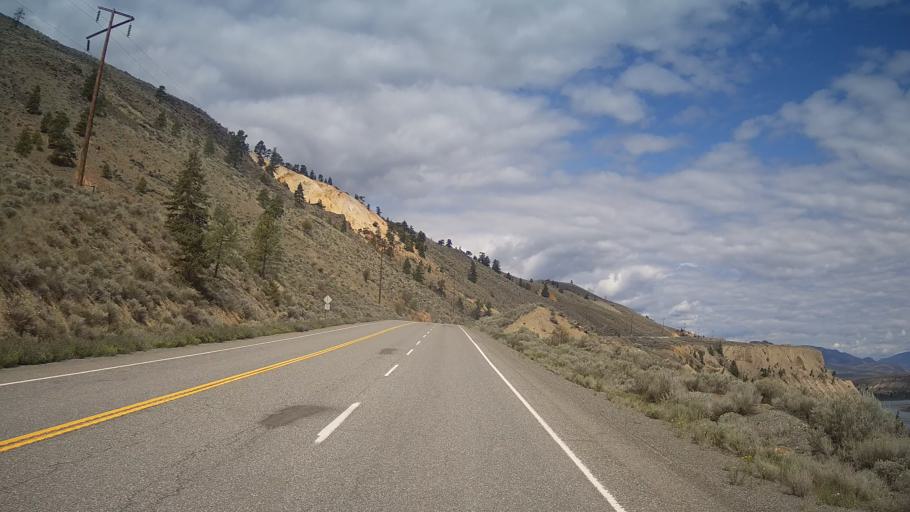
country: CA
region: British Columbia
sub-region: Thompson-Nicola Regional District
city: Ashcroft
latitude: 50.5532
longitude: -121.2981
